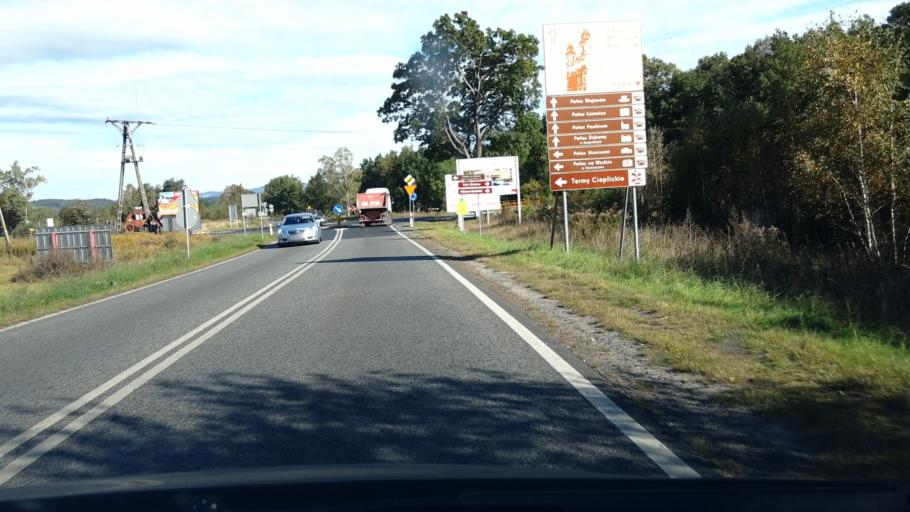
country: PL
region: Lower Silesian Voivodeship
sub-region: Powiat jeleniogorski
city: Karpacz
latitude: 50.8037
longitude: 15.7664
